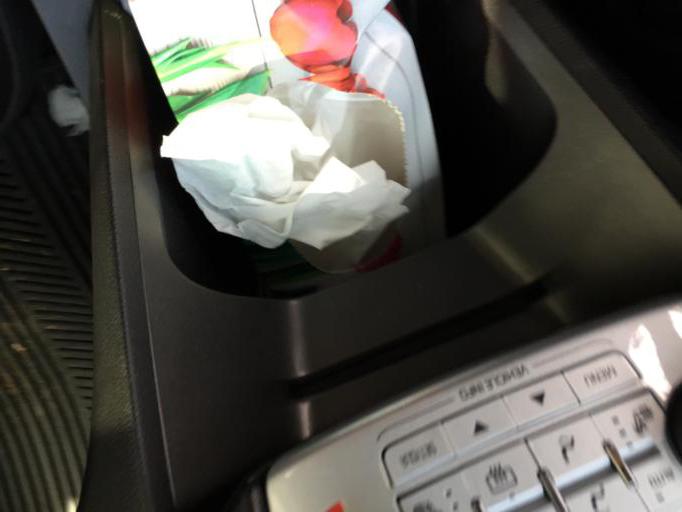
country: CA
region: British Columbia
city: Richmond
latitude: 49.1627
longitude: -123.1301
